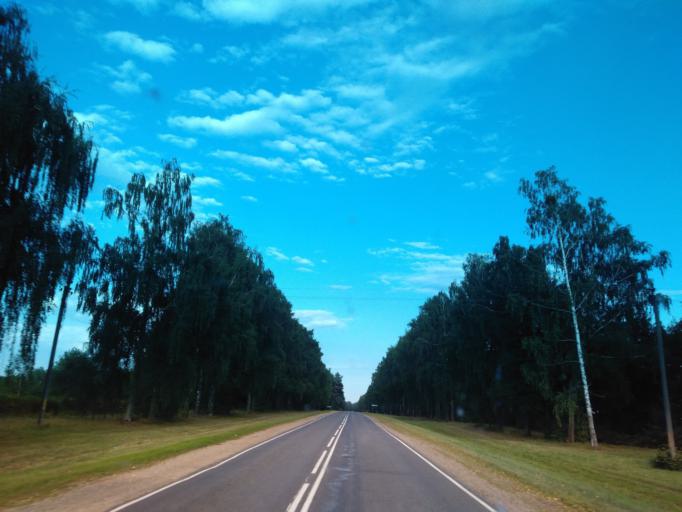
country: BY
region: Minsk
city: Uzda
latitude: 53.4257
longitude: 27.3684
